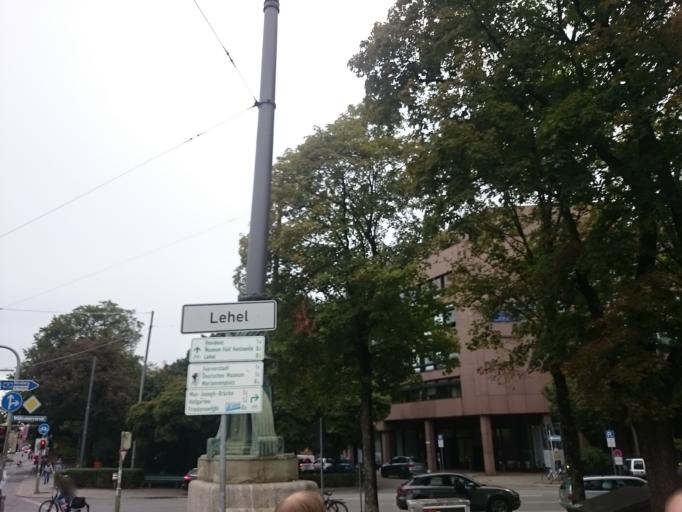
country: DE
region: Bavaria
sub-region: Upper Bavaria
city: Munich
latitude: 48.1372
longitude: 11.5903
